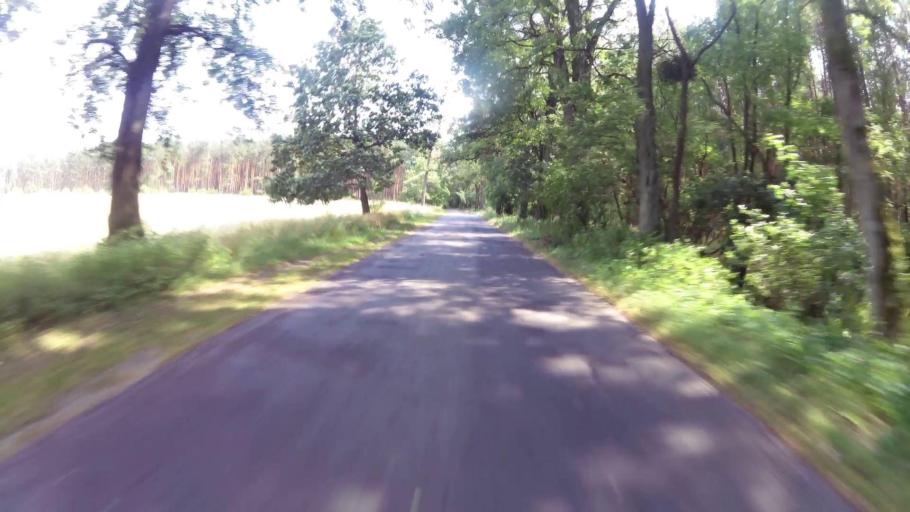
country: PL
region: West Pomeranian Voivodeship
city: Trzcinsko Zdroj
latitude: 52.8671
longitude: 14.6219
